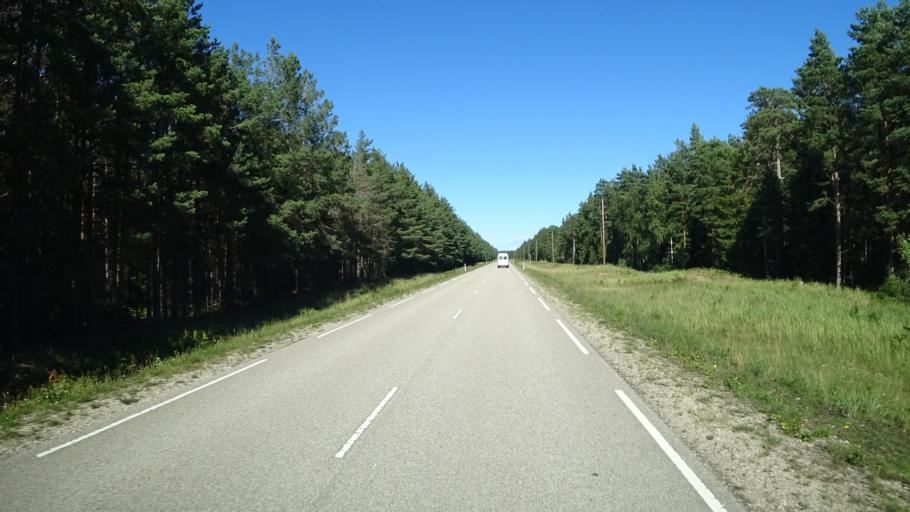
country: LV
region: Dundaga
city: Dundaga
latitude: 57.7298
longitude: 22.5069
